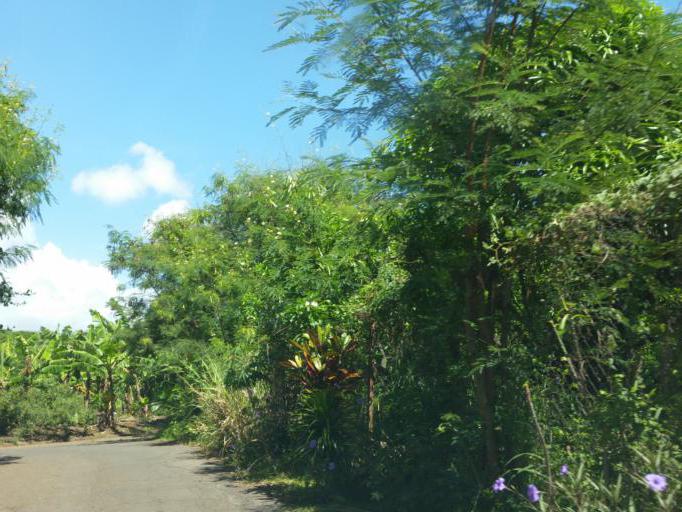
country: RE
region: Reunion
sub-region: Reunion
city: Sainte-Marie
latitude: -20.9057
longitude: 55.5151
